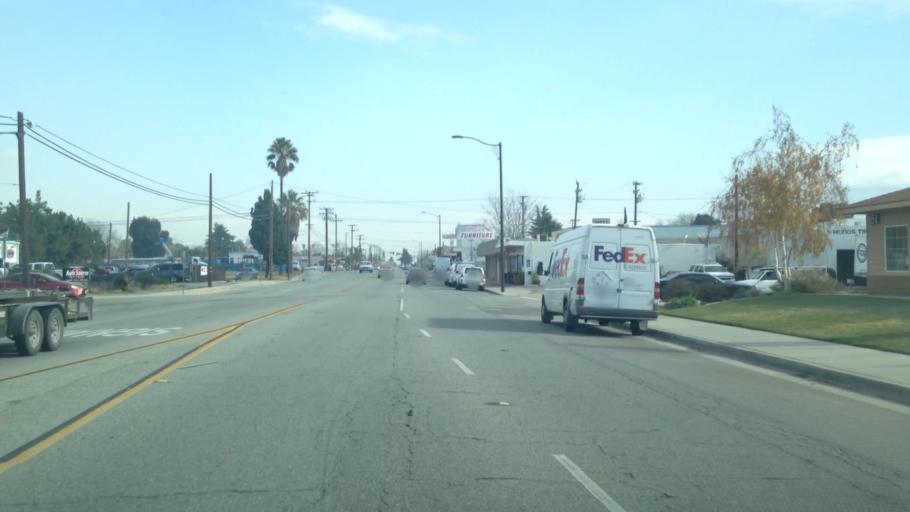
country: US
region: California
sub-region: Riverside County
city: Beaumont
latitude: 33.9294
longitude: -116.9708
